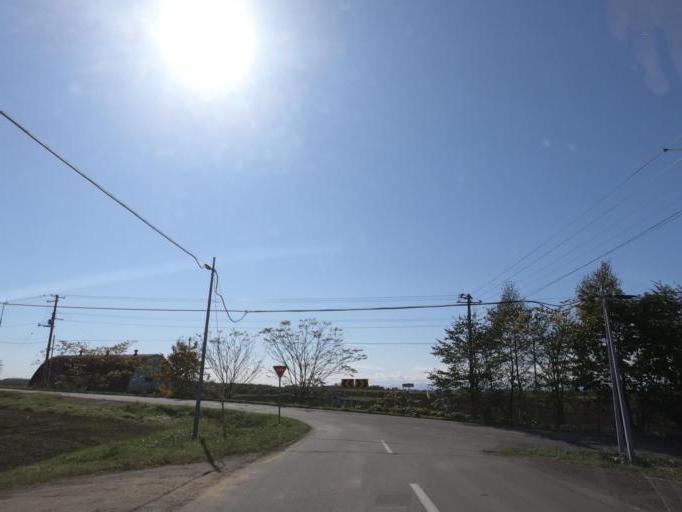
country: JP
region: Hokkaido
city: Obihiro
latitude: 42.8074
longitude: 143.2542
